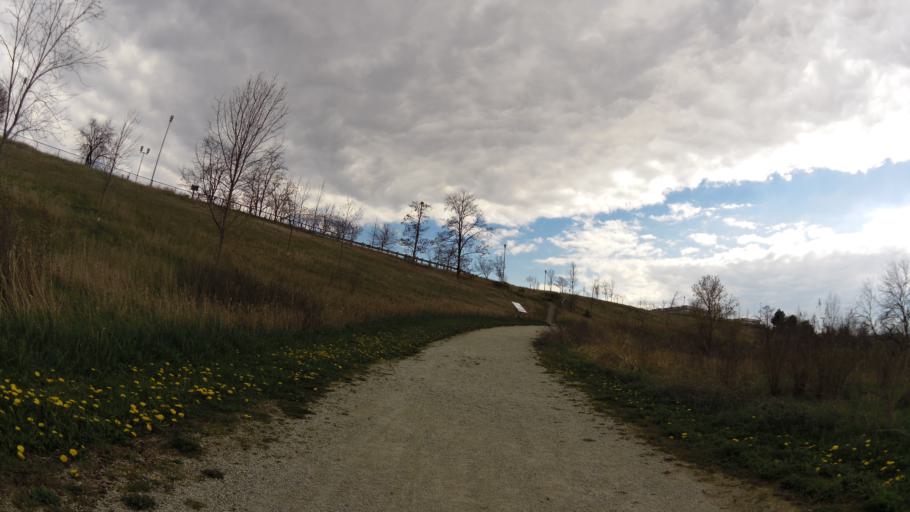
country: CA
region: Ontario
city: Etobicoke
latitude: 43.6689
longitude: -79.6556
